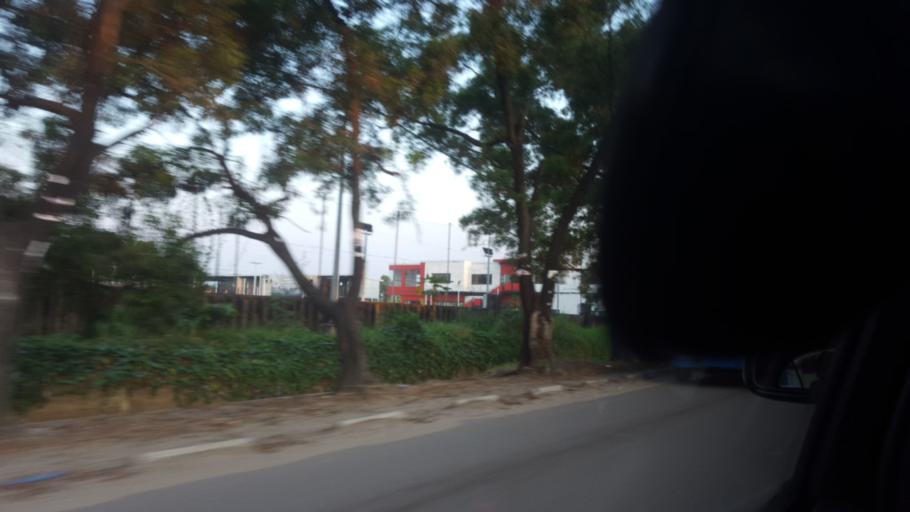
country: CD
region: Kinshasa
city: Kinshasa
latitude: -4.3392
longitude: 15.3204
